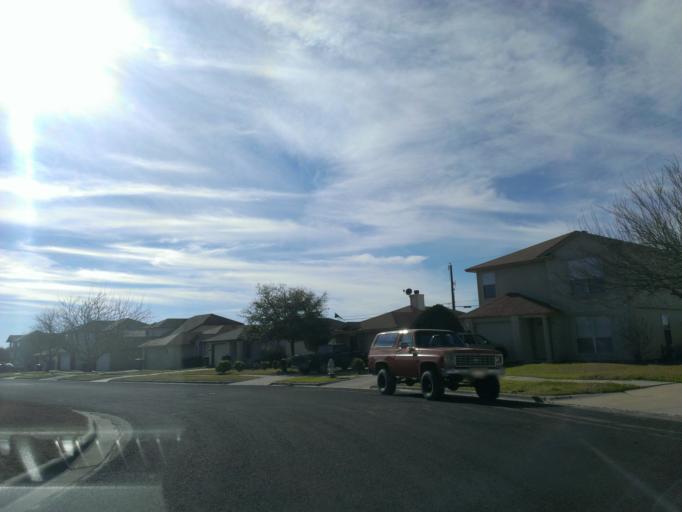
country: US
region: Texas
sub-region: Bell County
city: Killeen
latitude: 31.1405
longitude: -97.6974
